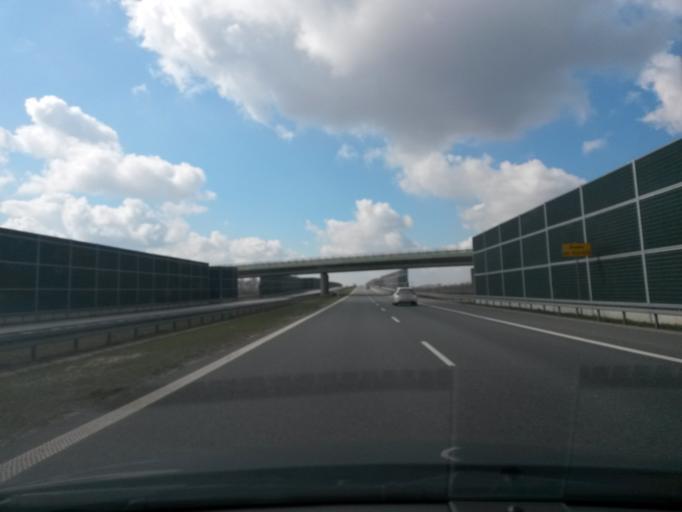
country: PL
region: Masovian Voivodeship
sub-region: Powiat zyrardowski
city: Wiskitki
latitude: 52.0973
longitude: 20.4005
